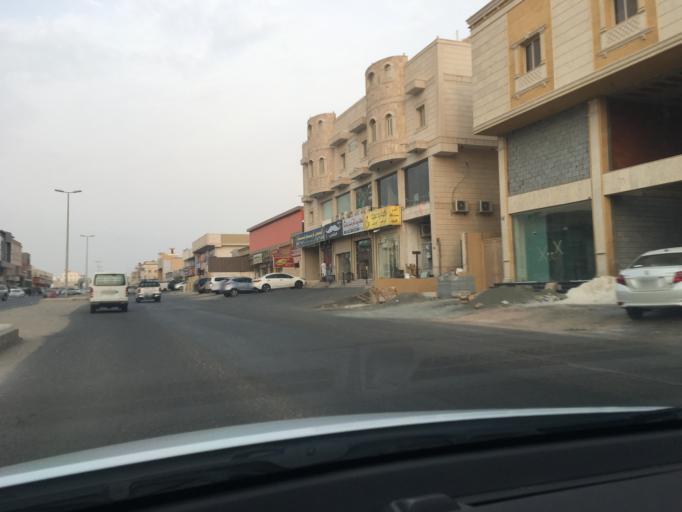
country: SA
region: Makkah
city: Jeddah
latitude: 21.7589
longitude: 39.1908
